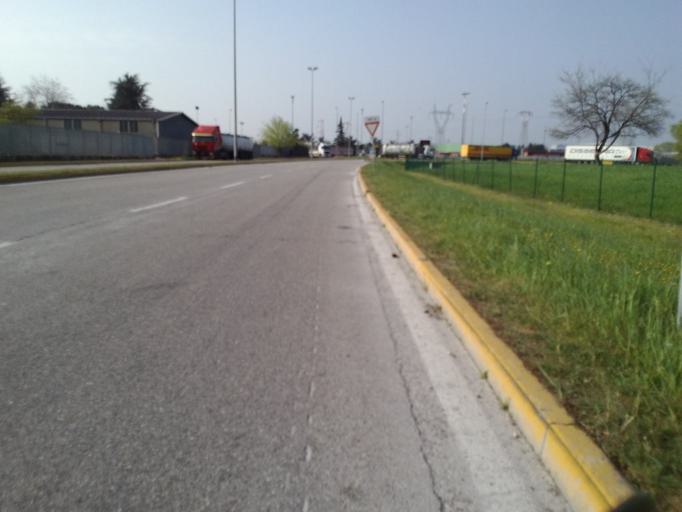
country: IT
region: Veneto
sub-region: Provincia di Verona
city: Dossobuono
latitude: 45.4155
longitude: 10.9231
